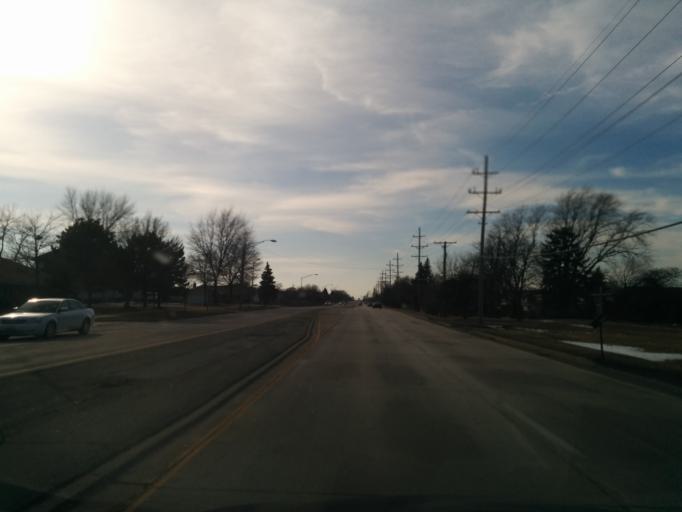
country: US
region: Illinois
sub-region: Cook County
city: Orland Hills
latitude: 41.5800
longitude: -87.8242
